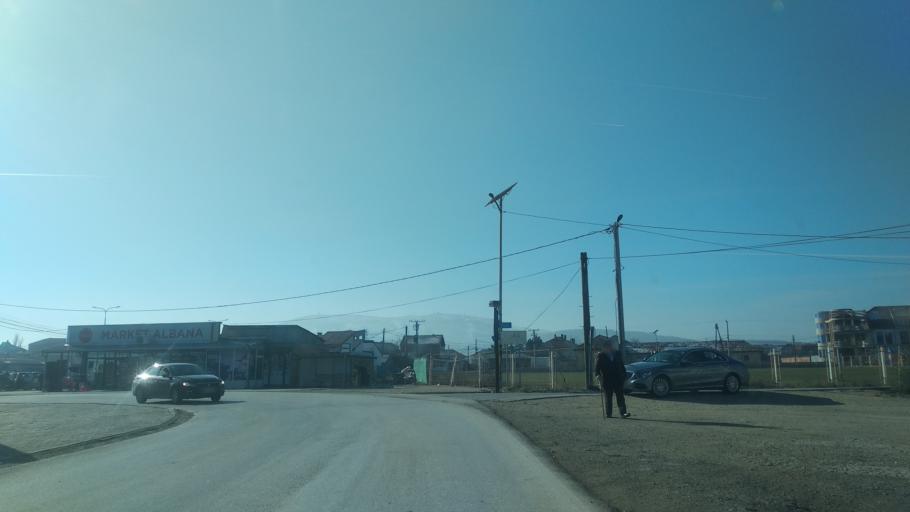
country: XK
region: Pristina
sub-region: Komuna e Gracanices
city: Glanica
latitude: 42.6005
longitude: 21.0233
